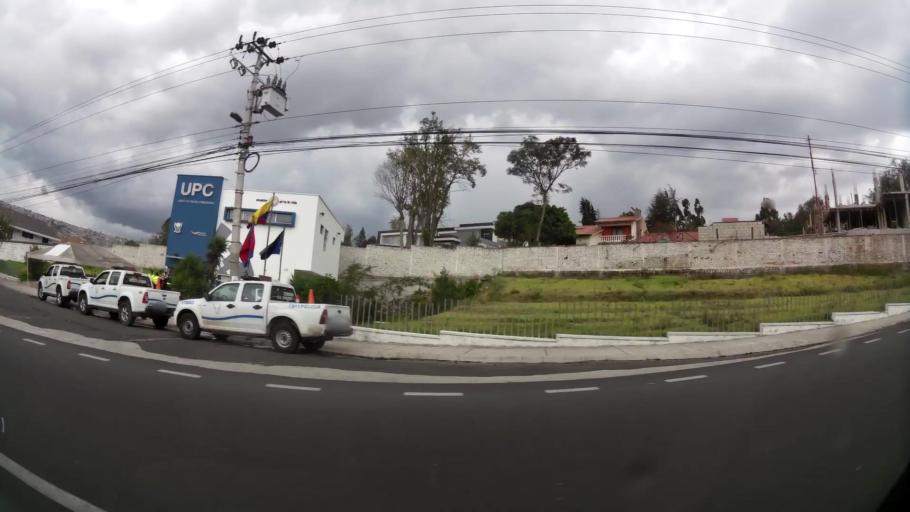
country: EC
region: Pichincha
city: Quito
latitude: -0.0666
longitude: -78.4584
